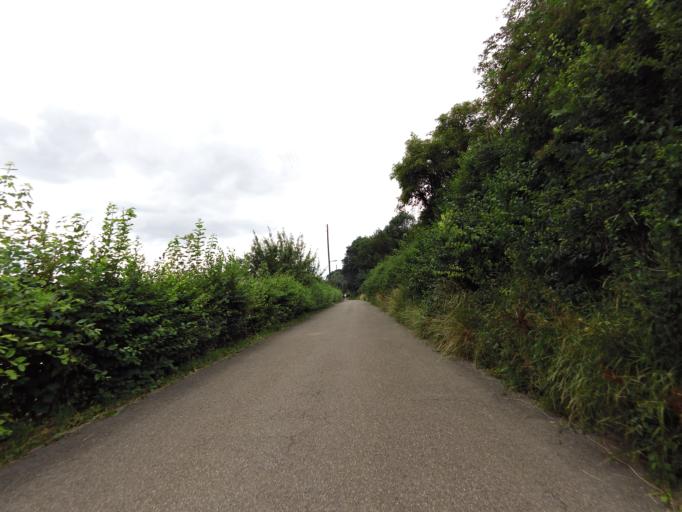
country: CH
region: Zurich
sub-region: Bezirk Zuerich
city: Zuerich (Kreis 10) / Wipkingen
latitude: 47.3986
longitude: 8.5284
